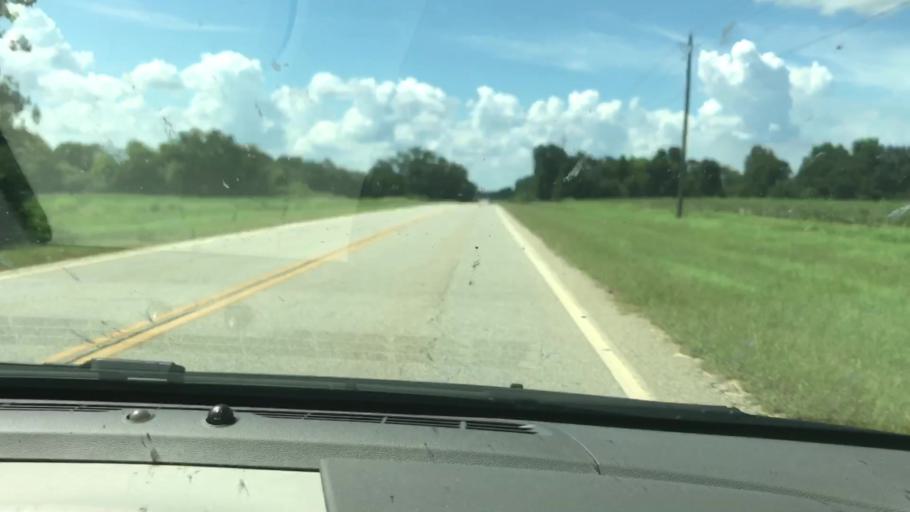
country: US
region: Georgia
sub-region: Quitman County
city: Georgetown
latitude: 31.7557
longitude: -85.0622
